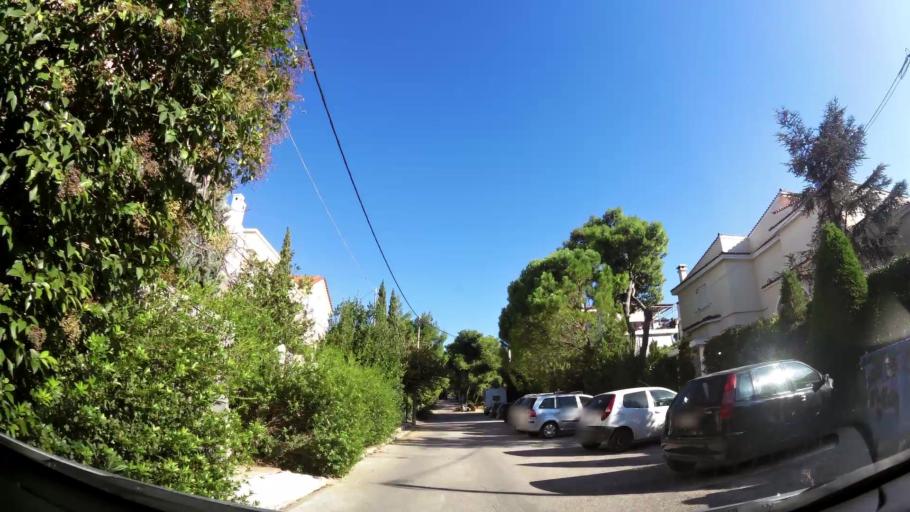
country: GR
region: Attica
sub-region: Nomarchia Athinas
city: Nea Erythraia
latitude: 38.0970
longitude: 23.8187
